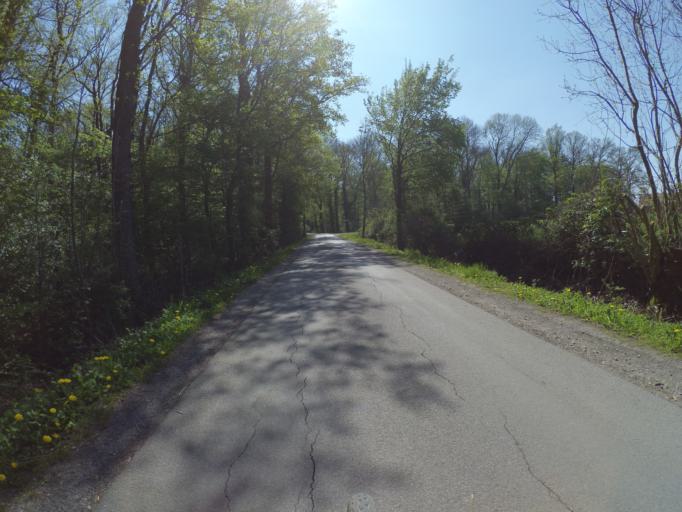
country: DE
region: North Rhine-Westphalia
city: Ludinghausen
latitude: 51.7589
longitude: 7.4400
